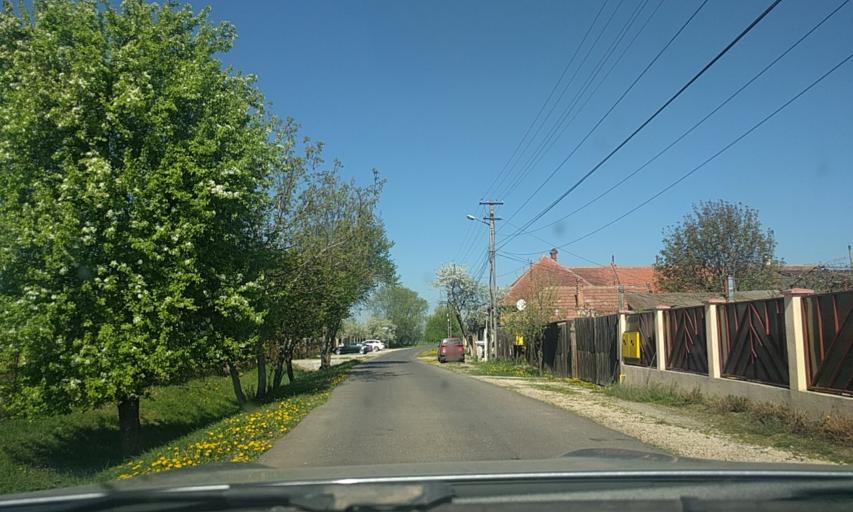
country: RO
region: Brasov
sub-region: Comuna Bod
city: Colonia Bod
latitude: 45.7152
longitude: 25.5749
